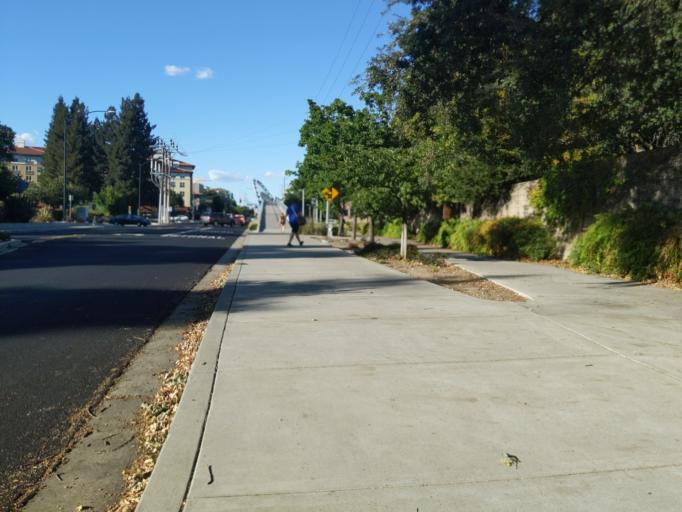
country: US
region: California
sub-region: Contra Costa County
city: Waldon
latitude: 37.9250
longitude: -122.0549
